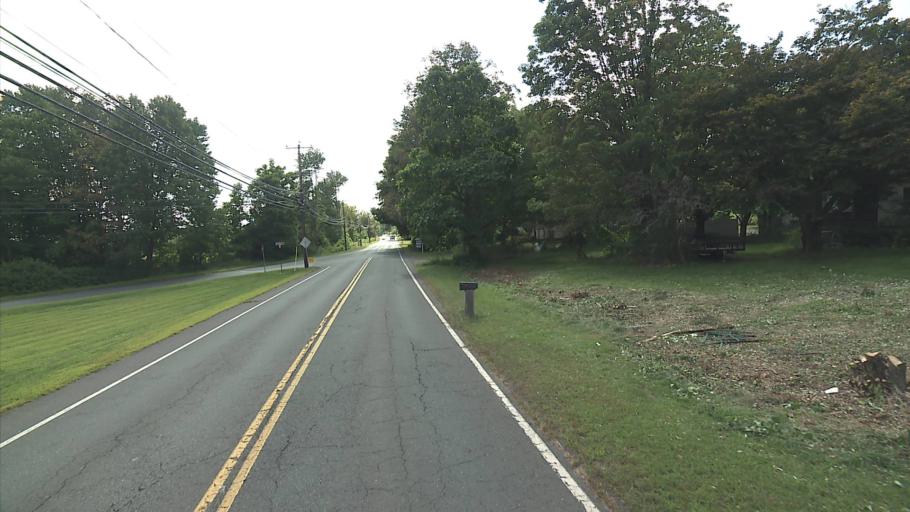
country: US
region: Connecticut
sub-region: Hartford County
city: Salmon Brook
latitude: 41.9734
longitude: -72.8082
